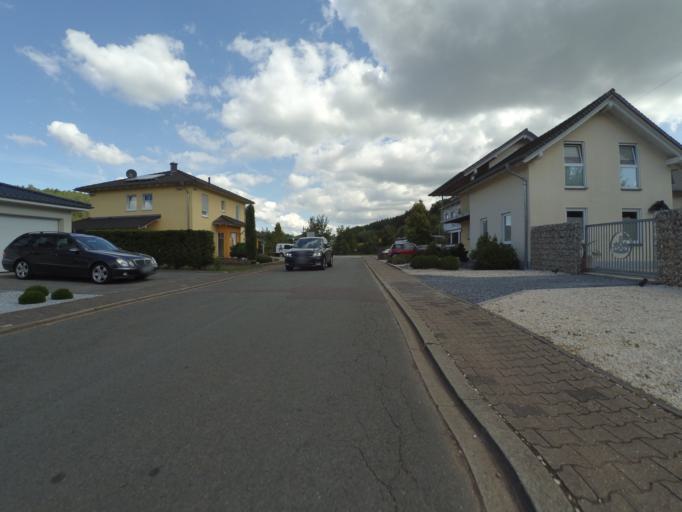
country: DE
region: Rheinland-Pfalz
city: Trassem
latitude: 49.5813
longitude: 6.5291
